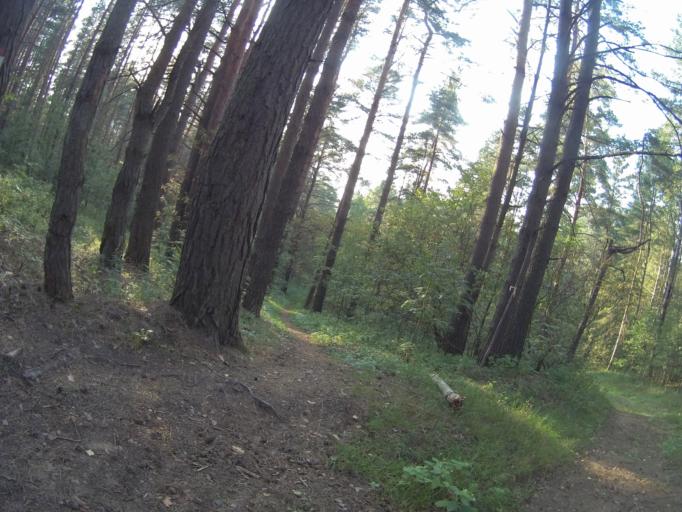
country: RU
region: Vladimir
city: Kommunar
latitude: 56.0689
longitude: 40.4374
